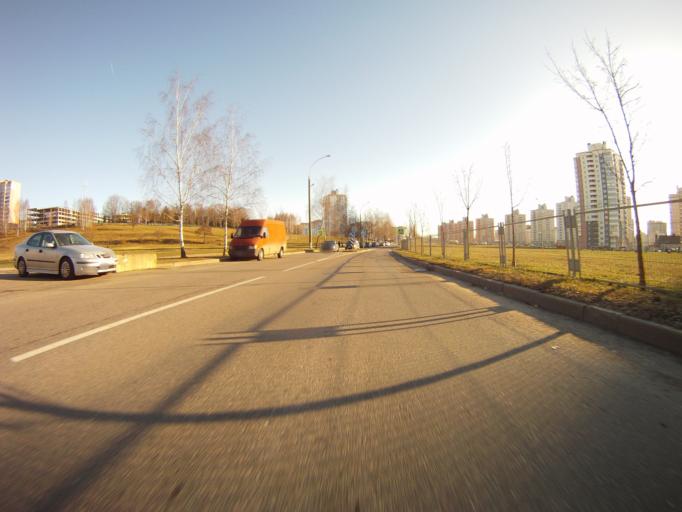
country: BY
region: Minsk
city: Novoye Medvezhino
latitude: 53.8794
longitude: 27.4451
